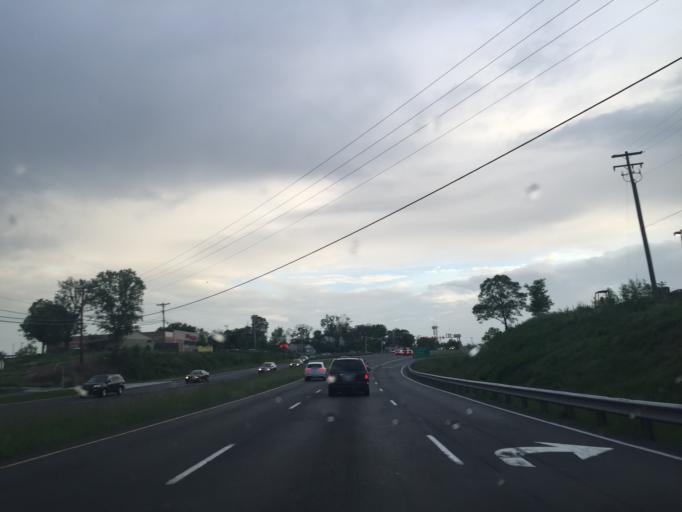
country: US
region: Virginia
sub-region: City of Winchester
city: Winchester
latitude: 39.1855
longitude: -78.1317
